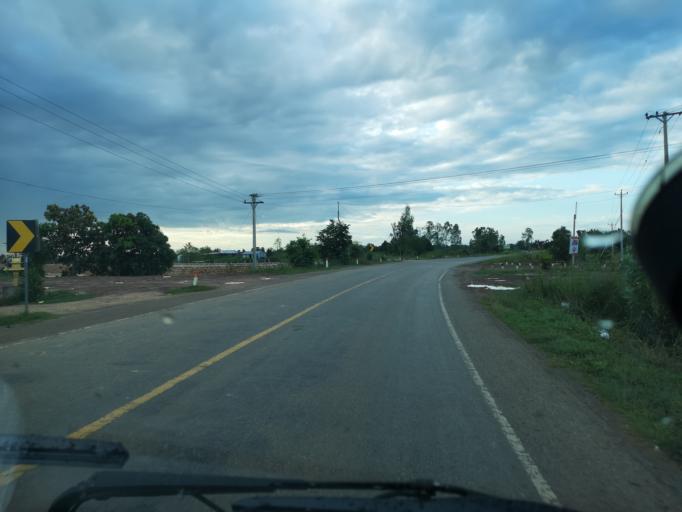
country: KH
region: Otar Meanchey
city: Samraong
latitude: 14.1608
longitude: 103.5199
